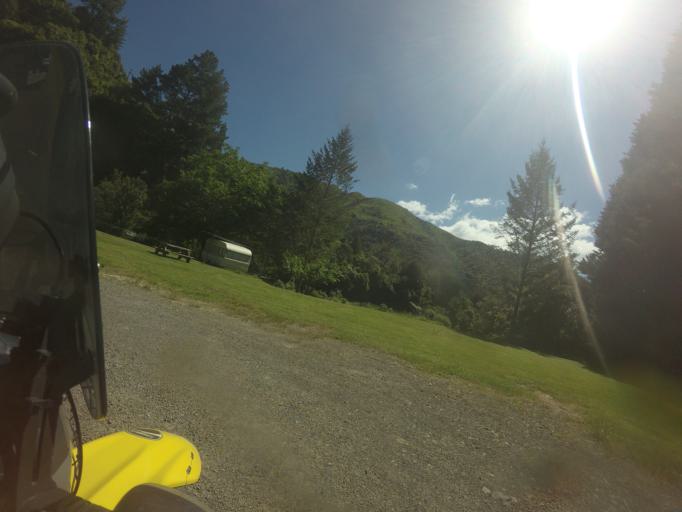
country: NZ
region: Bay of Plenty
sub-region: Opotiki District
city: Opotiki
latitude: -38.2778
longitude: 177.3442
